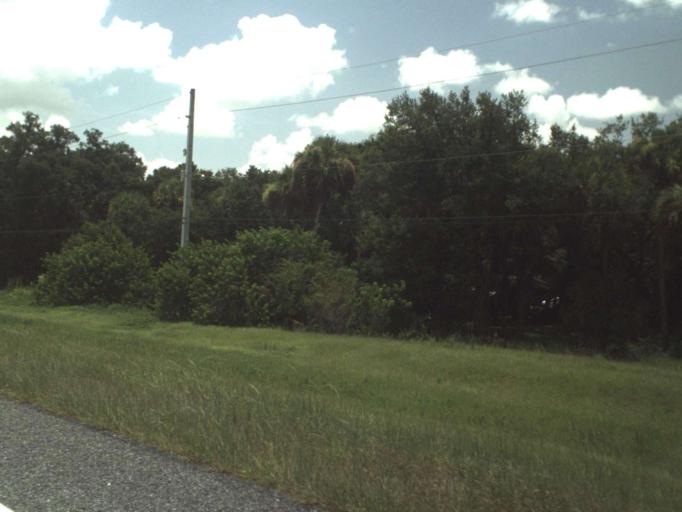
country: US
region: Florida
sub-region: Saint Lucie County
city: Fort Pierce South
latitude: 27.3689
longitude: -80.5573
